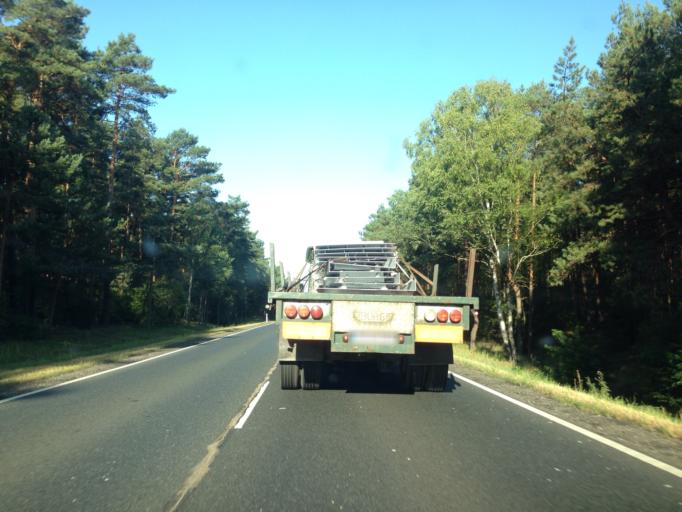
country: PL
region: Kujawsko-Pomorskie
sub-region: Bydgoszcz
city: Bydgoszcz
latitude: 53.0493
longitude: 18.0258
